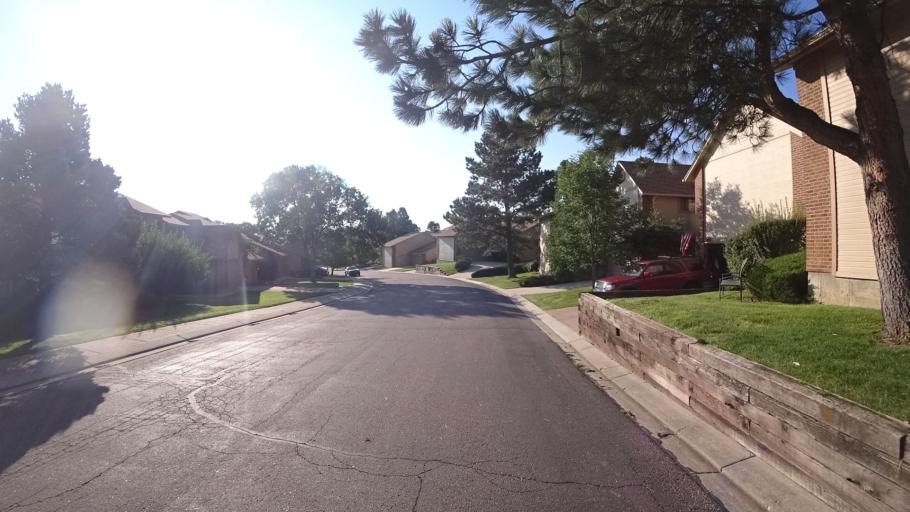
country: US
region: Colorado
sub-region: El Paso County
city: Colorado Springs
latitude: 38.8885
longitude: -104.8504
